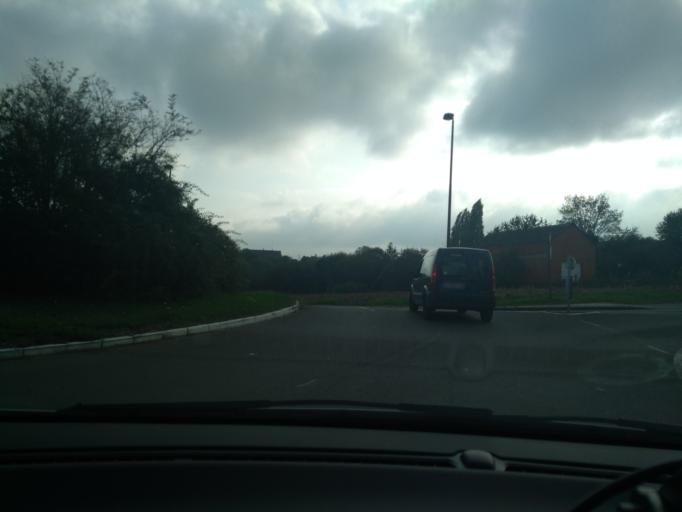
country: BE
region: Wallonia
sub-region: Province du Hainaut
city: Colfontaine
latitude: 50.4259
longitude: 3.8561
